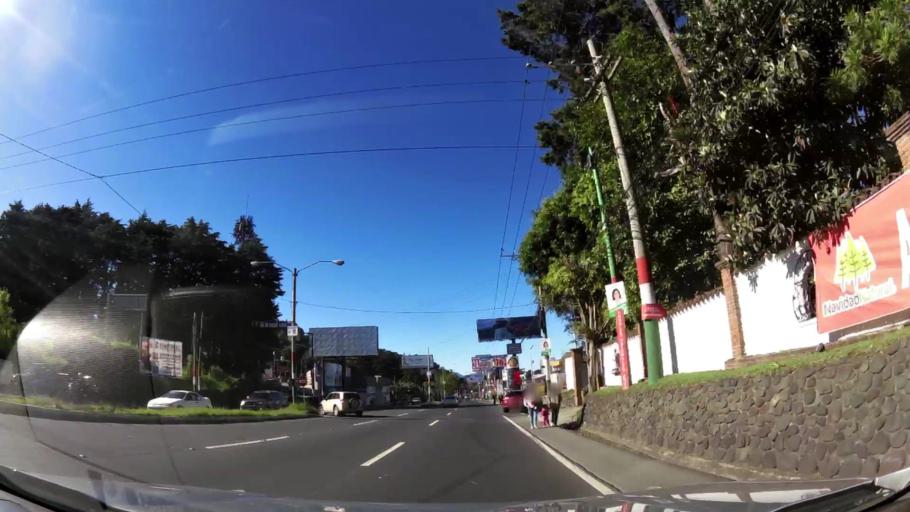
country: GT
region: Guatemala
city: San Jose Pinula
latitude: 14.5372
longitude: -90.4570
